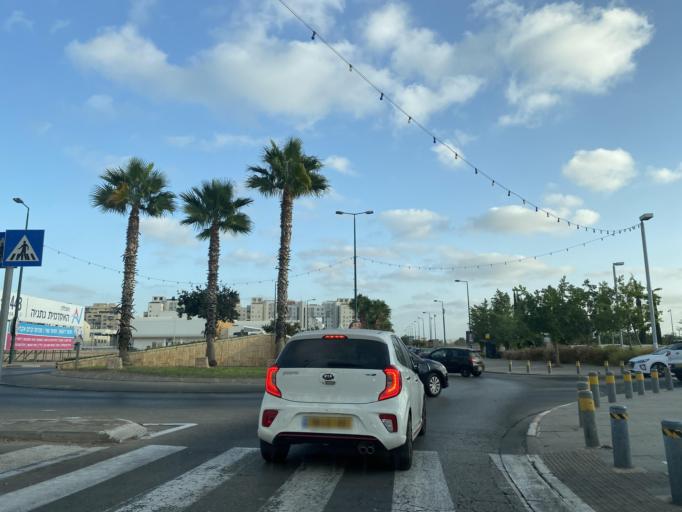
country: IL
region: Central District
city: Nordiyya
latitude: 32.3064
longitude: 34.8696
